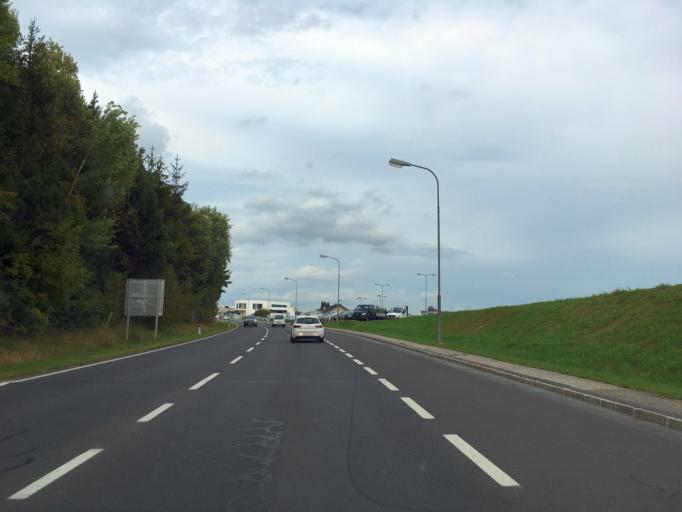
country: AT
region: Styria
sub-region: Politischer Bezirk Hartberg-Fuerstenfeld
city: Hartberg
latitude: 47.2844
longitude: 15.9777
